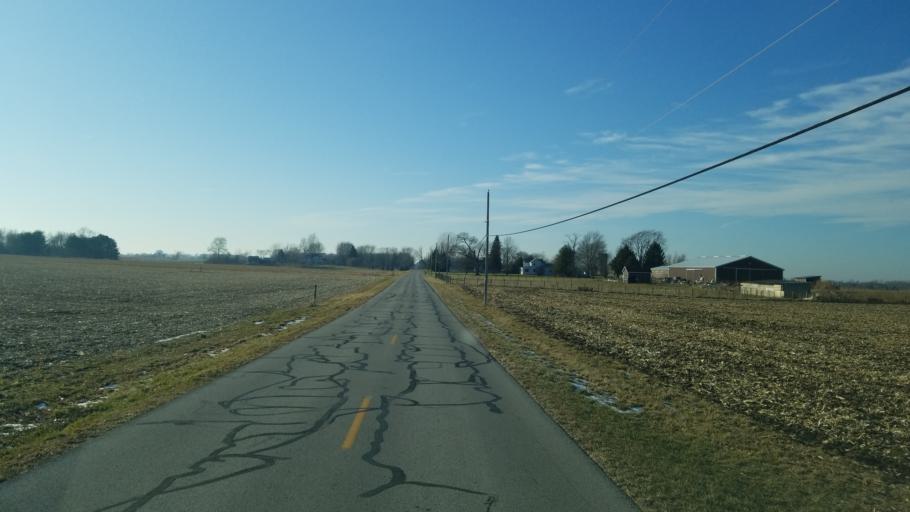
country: US
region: Ohio
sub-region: Sandusky County
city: Mount Carmel
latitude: 41.2705
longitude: -82.9490
